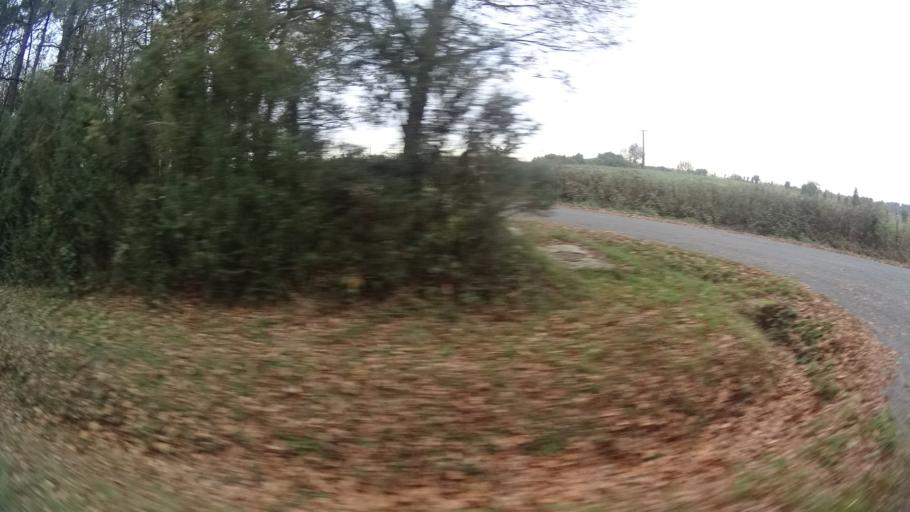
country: FR
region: Pays de la Loire
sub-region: Departement de la Loire-Atlantique
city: Avessac
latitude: 47.6607
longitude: -1.9401
